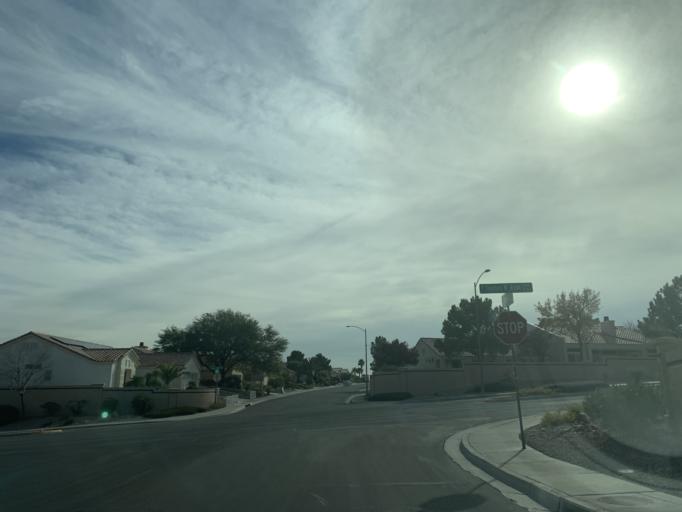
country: US
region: Nevada
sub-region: Clark County
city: Summerlin South
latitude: 36.2130
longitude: -115.3252
